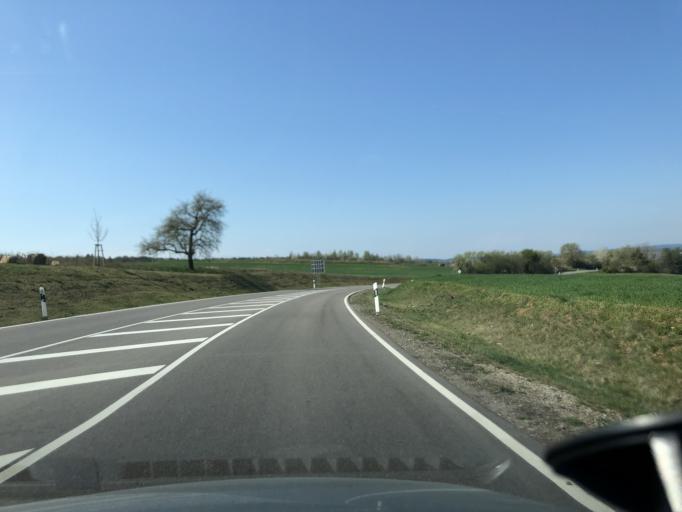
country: DE
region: Baden-Wuerttemberg
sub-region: Karlsruhe Region
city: Heimsheim
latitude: 48.8111
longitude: 8.8907
